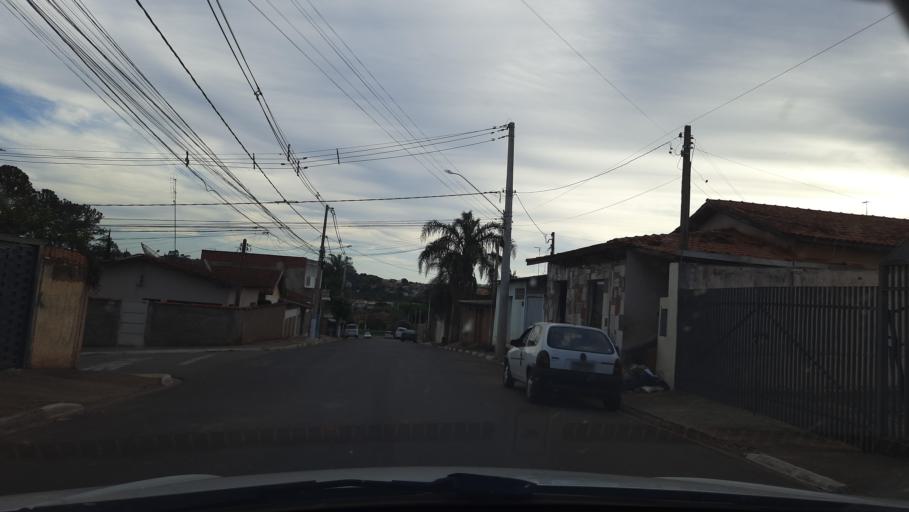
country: BR
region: Sao Paulo
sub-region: Casa Branca
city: Casa Branca
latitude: -21.7661
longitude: -47.0872
